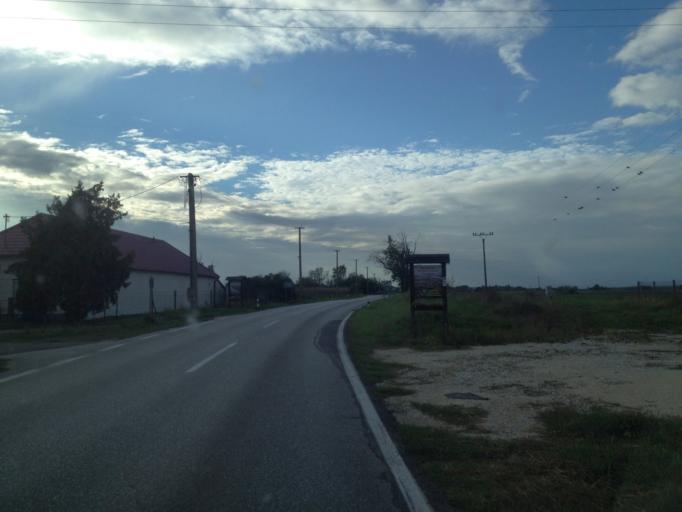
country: HU
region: Komarom-Esztergom
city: Dunaalmas
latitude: 47.7456
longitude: 18.3372
